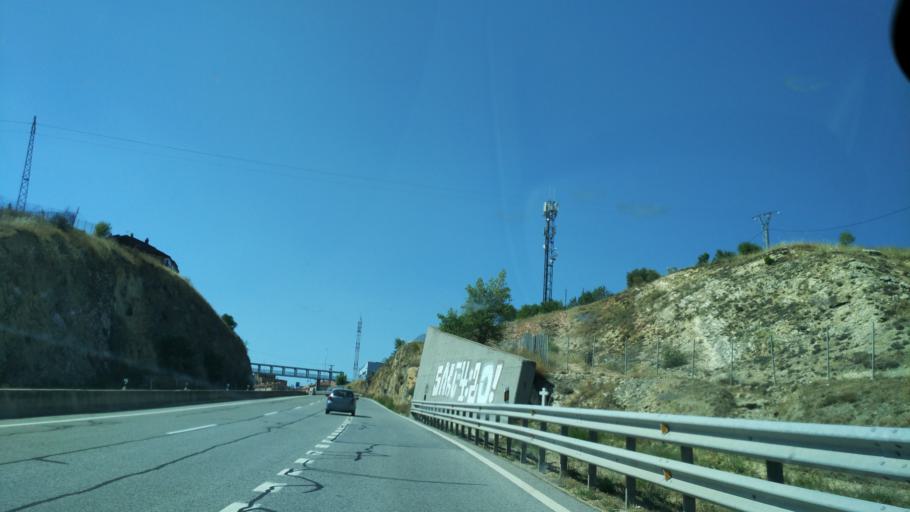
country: ES
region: Madrid
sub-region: Provincia de Madrid
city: El Molar
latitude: 40.7274
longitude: -3.5791
